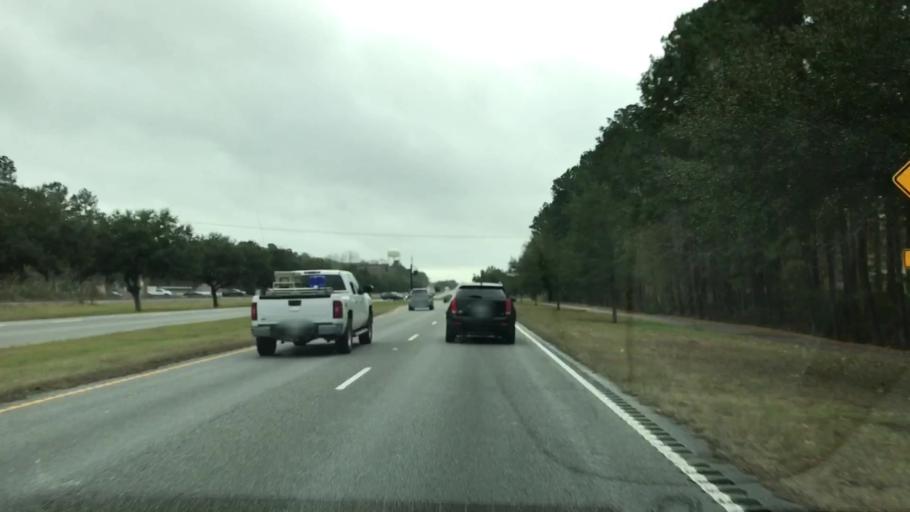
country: US
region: South Carolina
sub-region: Berkeley County
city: Goose Creek
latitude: 33.0132
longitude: -80.0368
